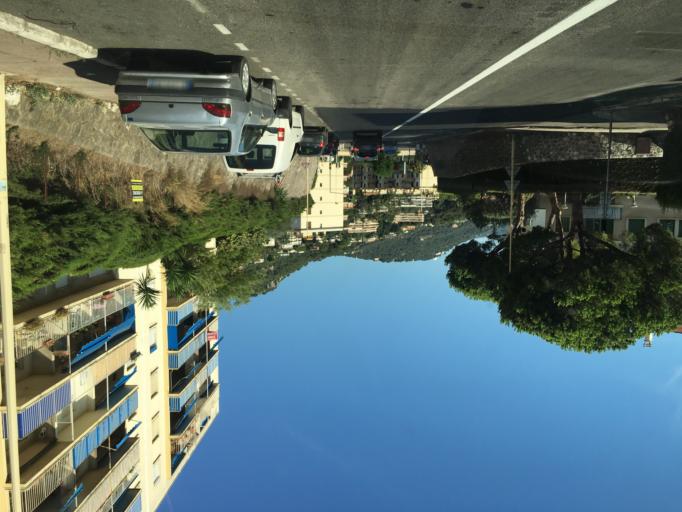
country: FR
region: Provence-Alpes-Cote d'Azur
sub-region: Departement des Alpes-Maritimes
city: Villefranche-sur-Mer
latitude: 43.7010
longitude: 7.2943
